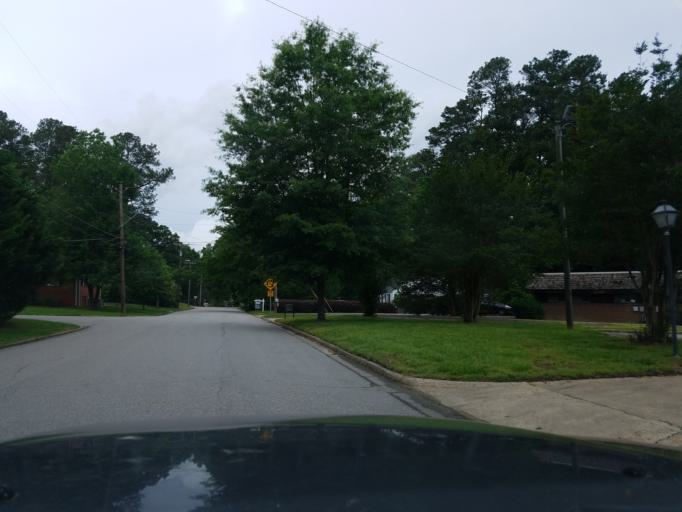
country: US
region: North Carolina
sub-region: Durham County
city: Durham
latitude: 36.0234
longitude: -78.9195
